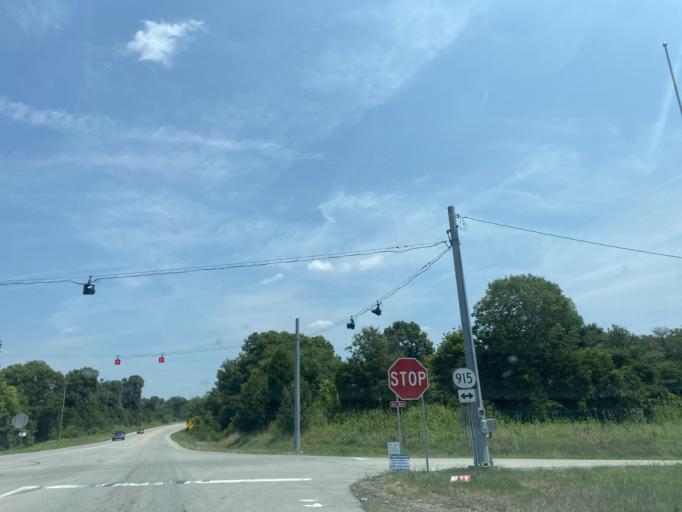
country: US
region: Kentucky
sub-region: Campbell County
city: Claryville
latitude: 38.9378
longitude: -84.4099
